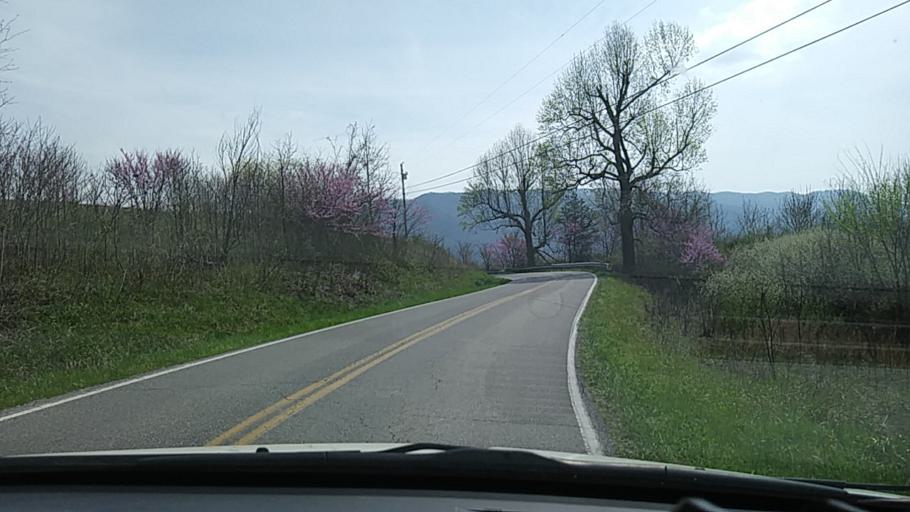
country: US
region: Tennessee
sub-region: Greene County
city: Tusculum
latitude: 36.0916
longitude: -82.7278
